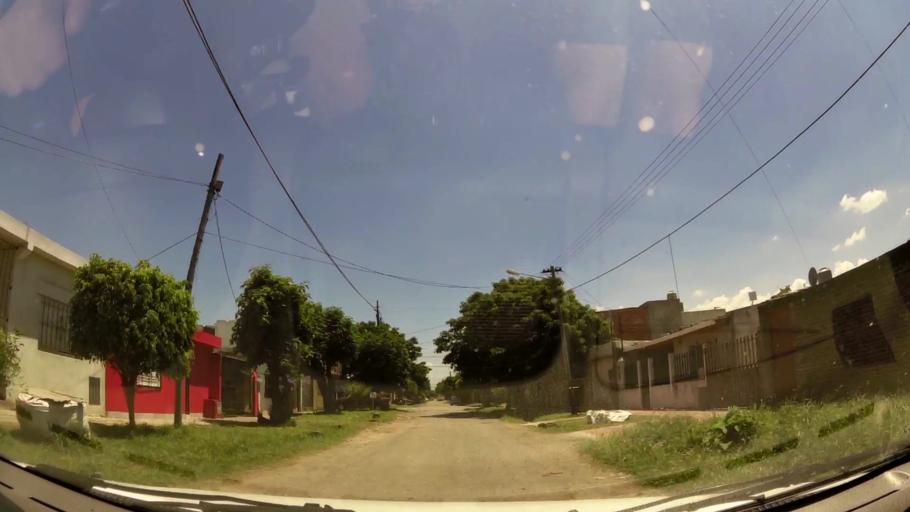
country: AR
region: Buenos Aires
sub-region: Partido de Merlo
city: Merlo
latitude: -34.6467
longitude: -58.7078
